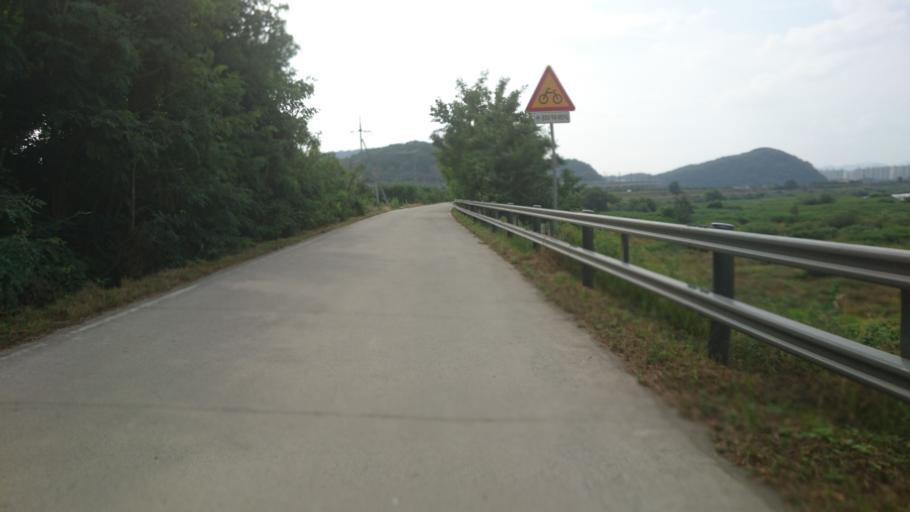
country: KR
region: Gyeongsangbuk-do
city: Gyeongsan-si
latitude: 35.8586
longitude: 128.6821
